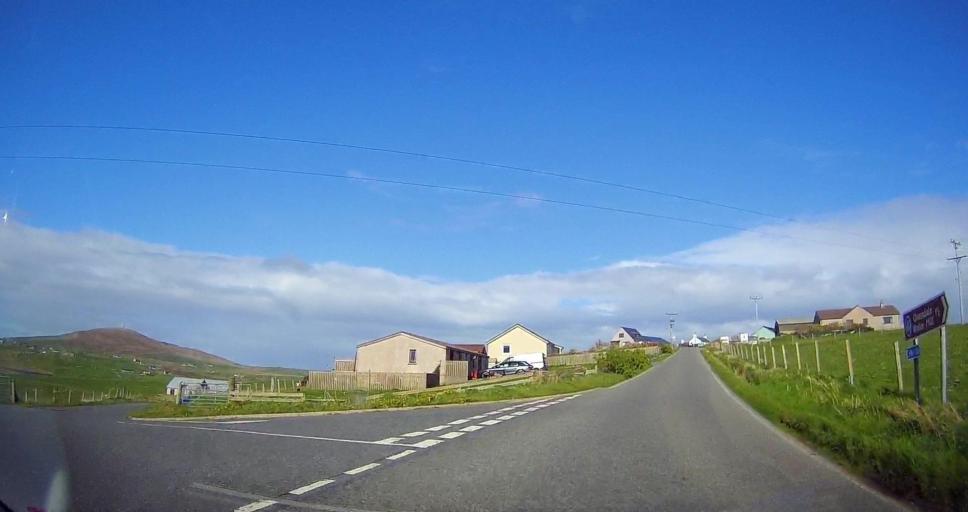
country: GB
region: Scotland
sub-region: Shetland Islands
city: Sandwick
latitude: 59.9159
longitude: -1.3214
